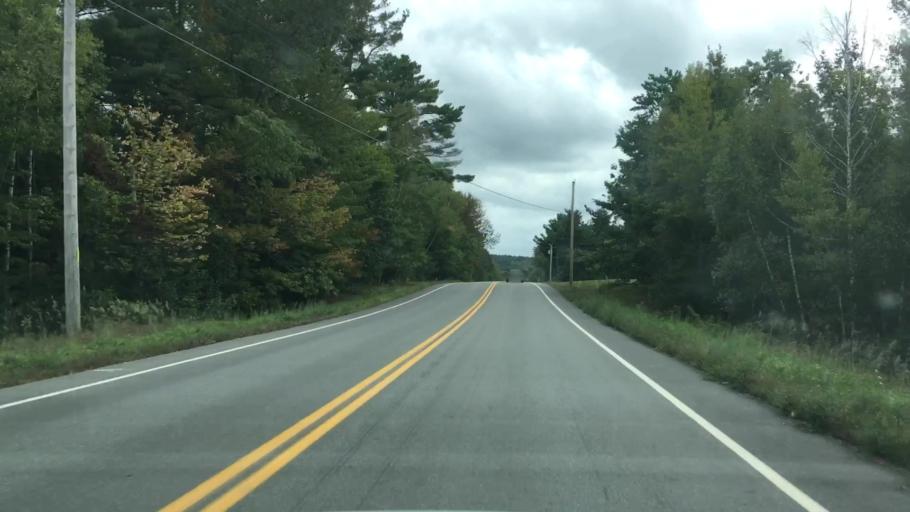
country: US
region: Maine
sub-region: Penobscot County
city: Hermon
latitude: 44.7539
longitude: -68.9720
